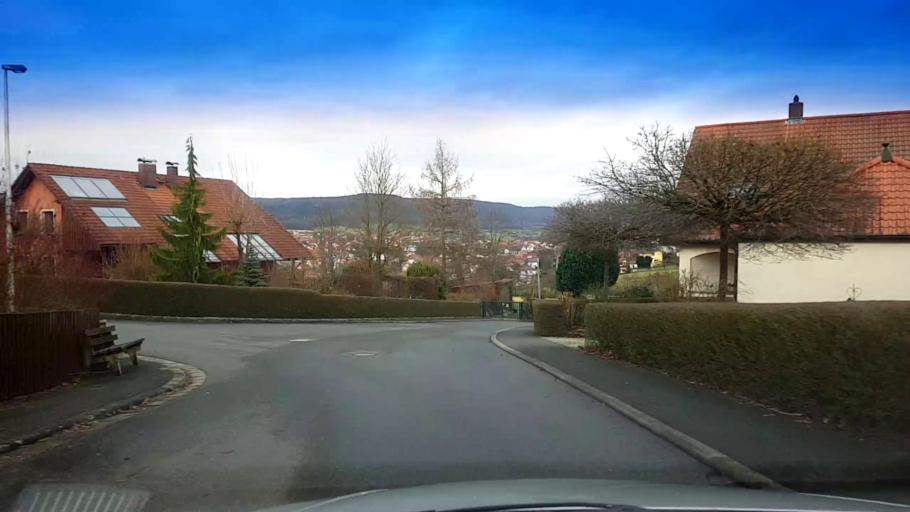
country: DE
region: Bavaria
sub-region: Upper Franconia
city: Litzendorf
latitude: 49.9066
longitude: 10.9943
